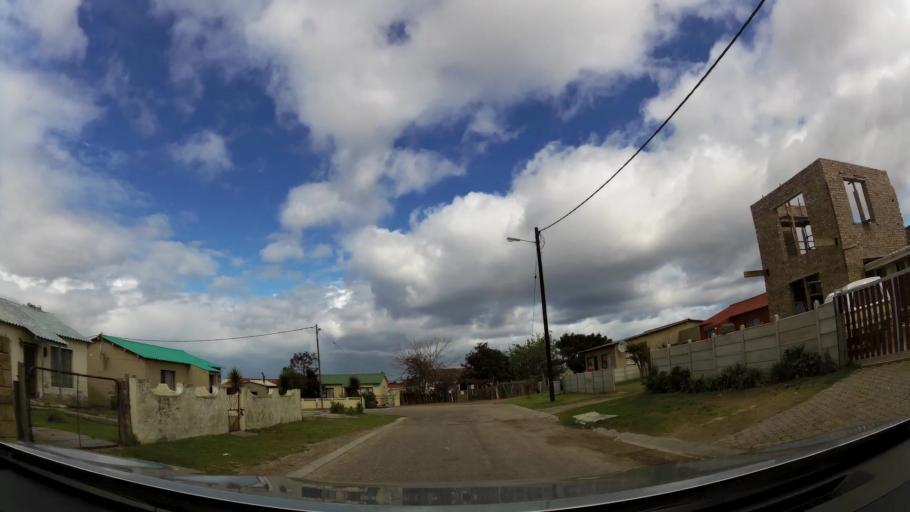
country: ZA
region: Western Cape
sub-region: Eden District Municipality
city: George
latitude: -34.0214
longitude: 22.4716
